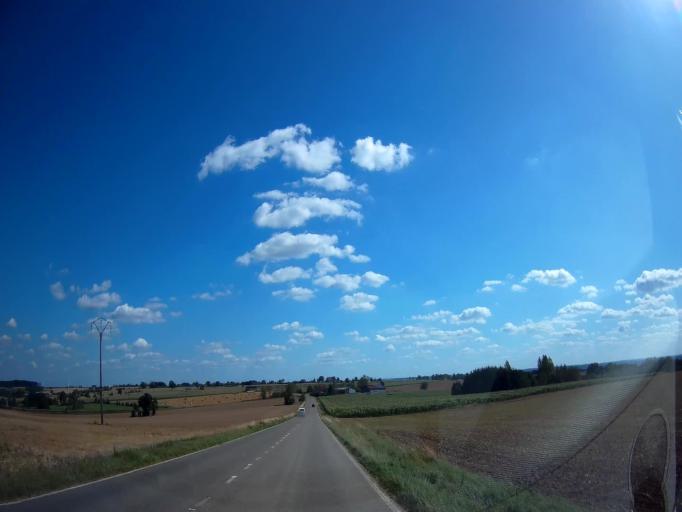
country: FR
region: Champagne-Ardenne
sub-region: Departement des Ardennes
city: Fromelennes
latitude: 50.1769
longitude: 4.8668
